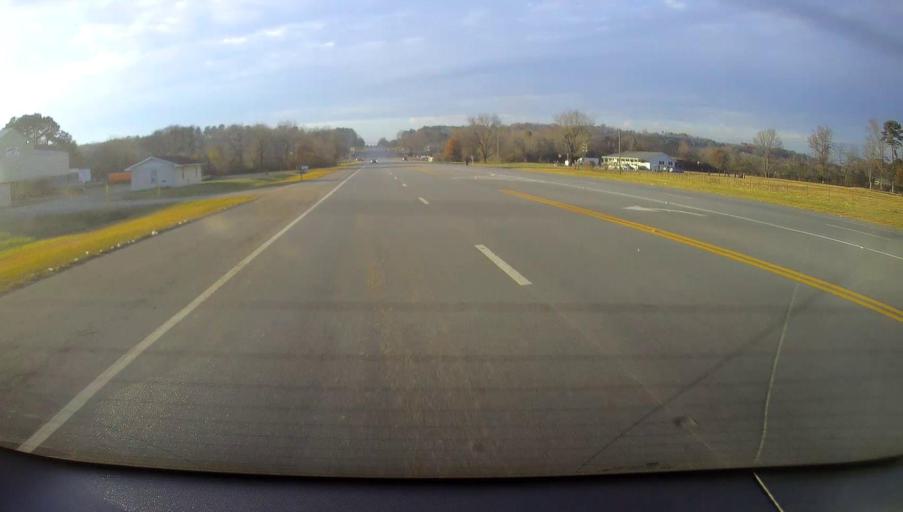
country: US
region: Alabama
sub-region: Blount County
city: Blountsville
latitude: 34.1648
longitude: -86.5123
